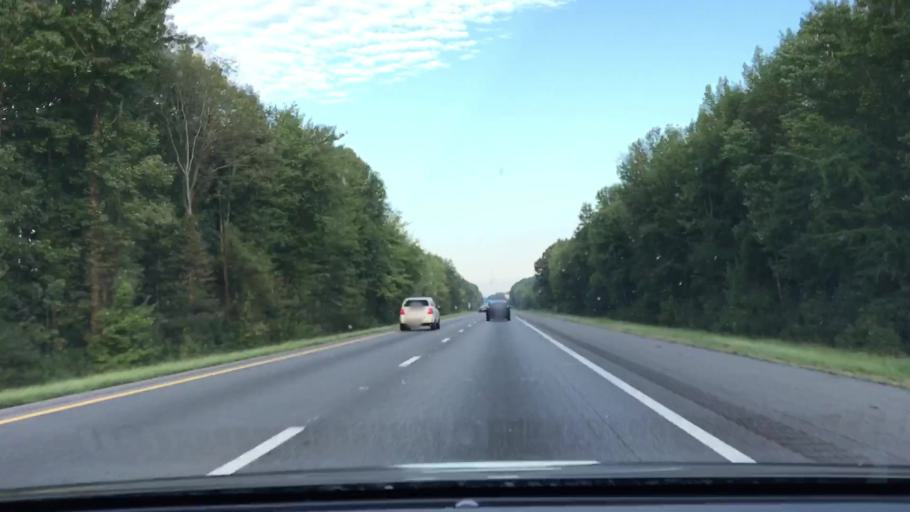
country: US
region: Kentucky
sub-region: Todd County
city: Guthrie
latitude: 36.4987
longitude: -87.1797
